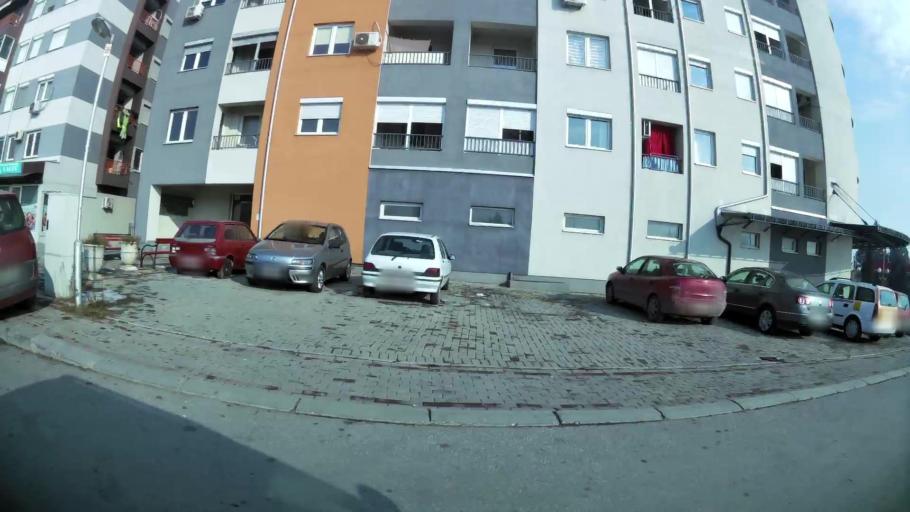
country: MK
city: Creshevo
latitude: 42.0055
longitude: 21.5013
